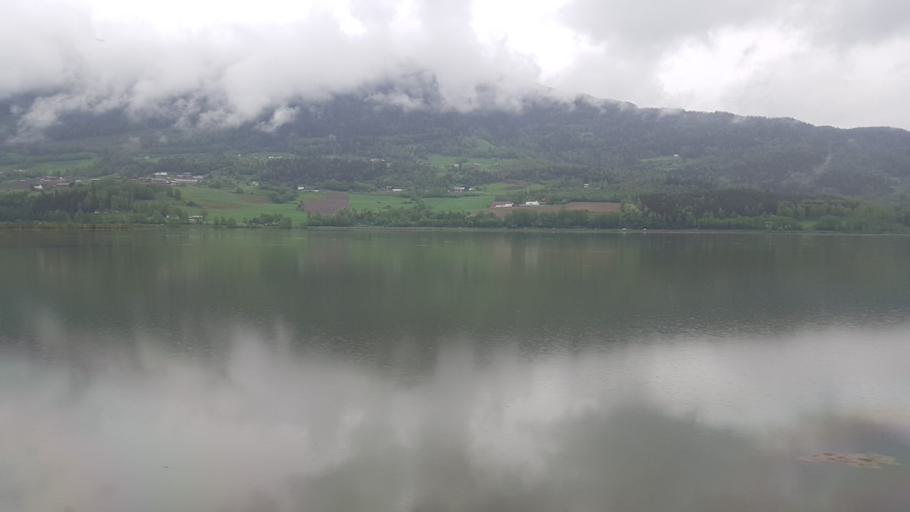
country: NO
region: Oppland
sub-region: Oyer
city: Tretten
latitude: 61.4137
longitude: 10.2358
